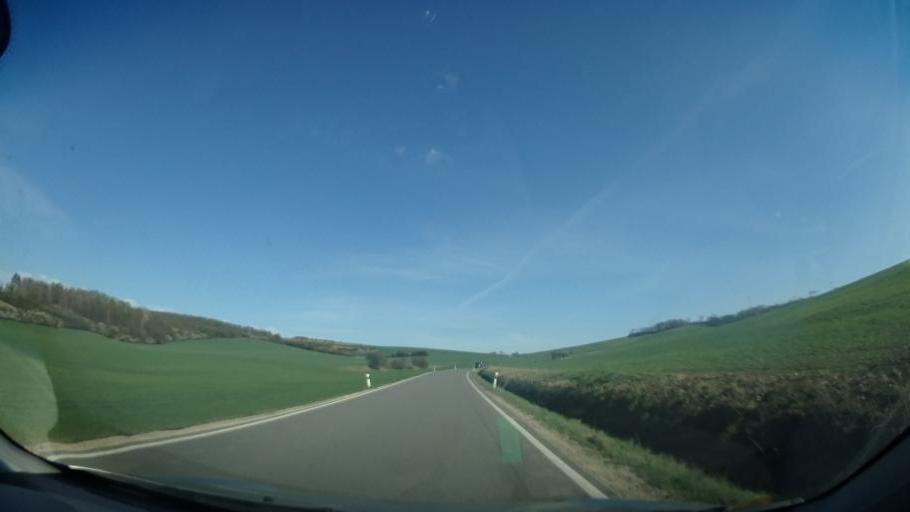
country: CZ
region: South Moravian
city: Ostopovice
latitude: 49.1548
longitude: 16.5542
